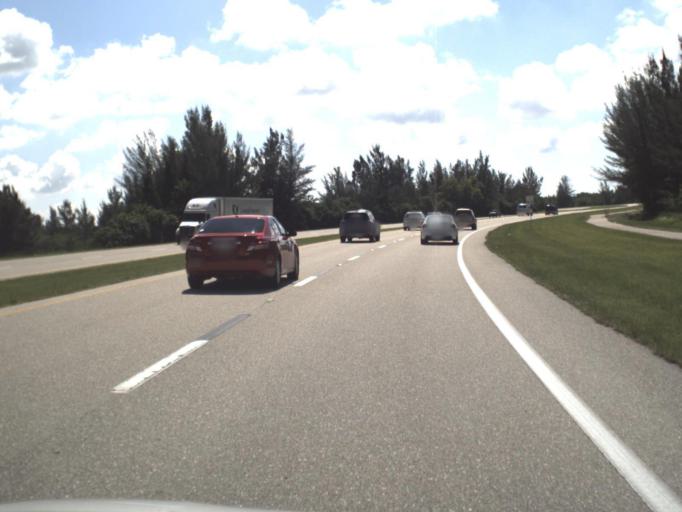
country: US
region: Florida
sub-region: Lee County
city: Pine Island Center
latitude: 26.6134
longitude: -82.0374
